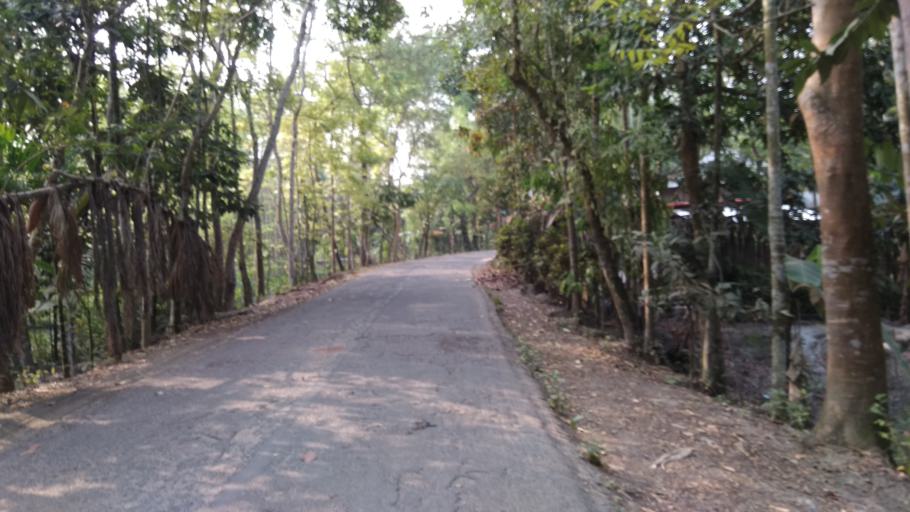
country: BD
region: Barisal
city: Mehendiganj
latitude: 22.9515
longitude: 90.4158
